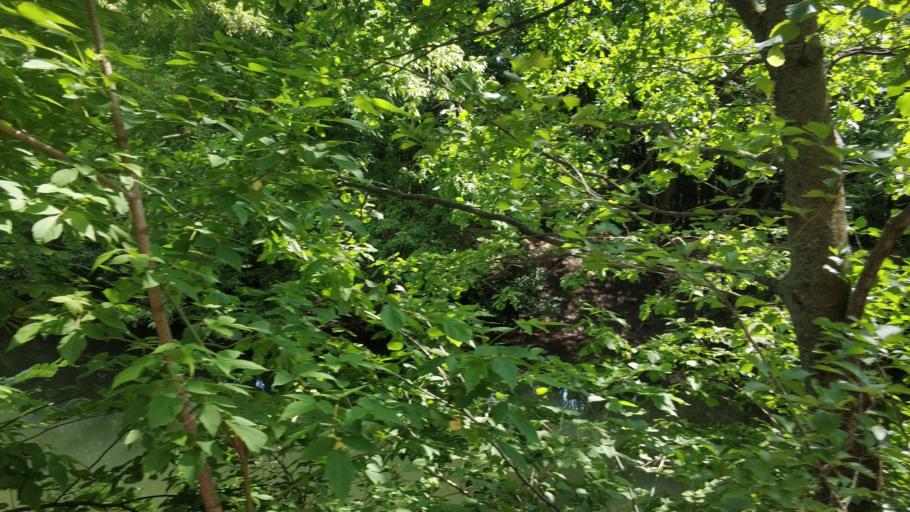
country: RU
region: Moscow
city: Perovo
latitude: 55.7329
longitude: 37.8052
